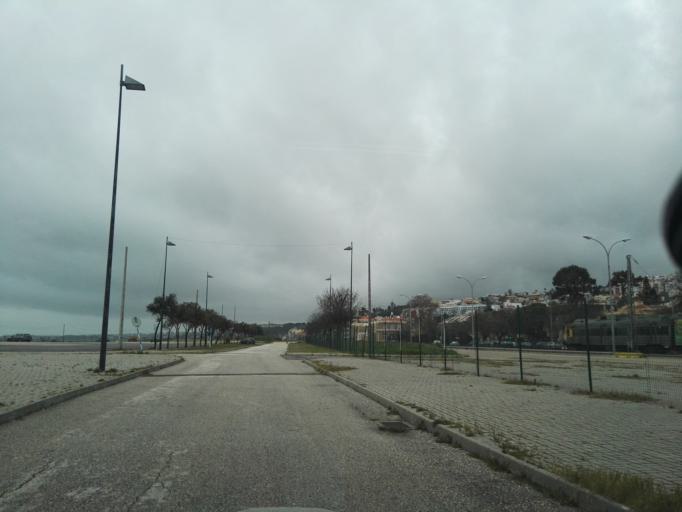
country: PT
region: Lisbon
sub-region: Oeiras
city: Alges
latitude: 38.6982
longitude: -9.2348
